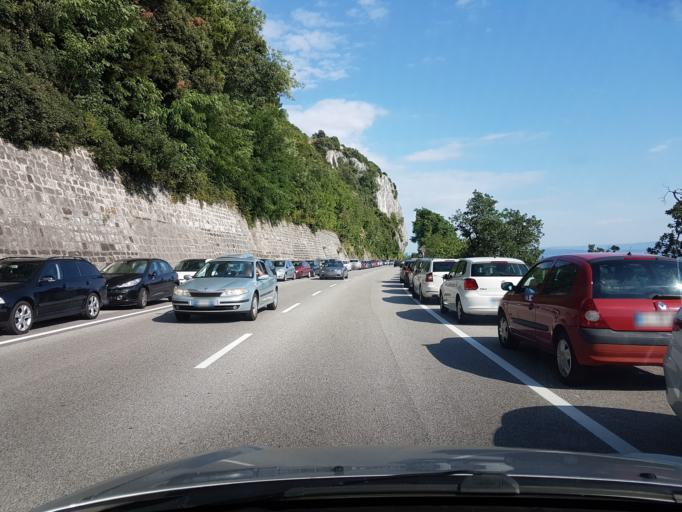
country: IT
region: Friuli Venezia Giulia
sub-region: Provincia di Trieste
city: Aurisina Cave
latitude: 45.7492
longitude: 13.6596
